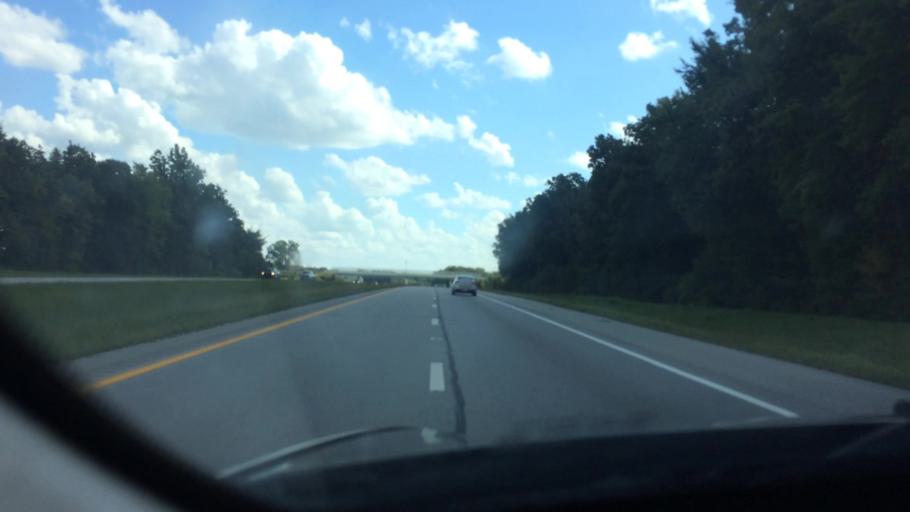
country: US
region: Ohio
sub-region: Shelby County
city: Anna
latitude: 40.4280
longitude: -84.1695
